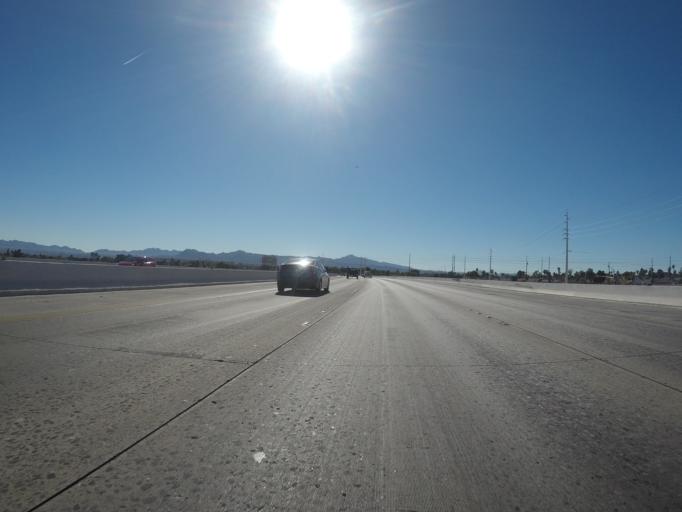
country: US
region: Nevada
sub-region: Clark County
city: Whitney
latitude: 36.1021
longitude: -115.0822
